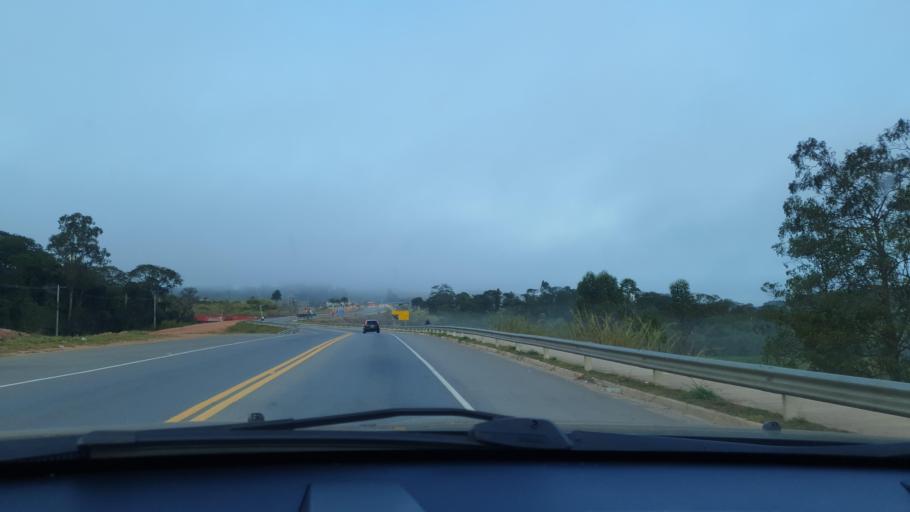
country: BR
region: Sao Paulo
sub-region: Vargem Grande Paulista
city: Vargem Grande Paulista
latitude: -23.6404
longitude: -47.0568
